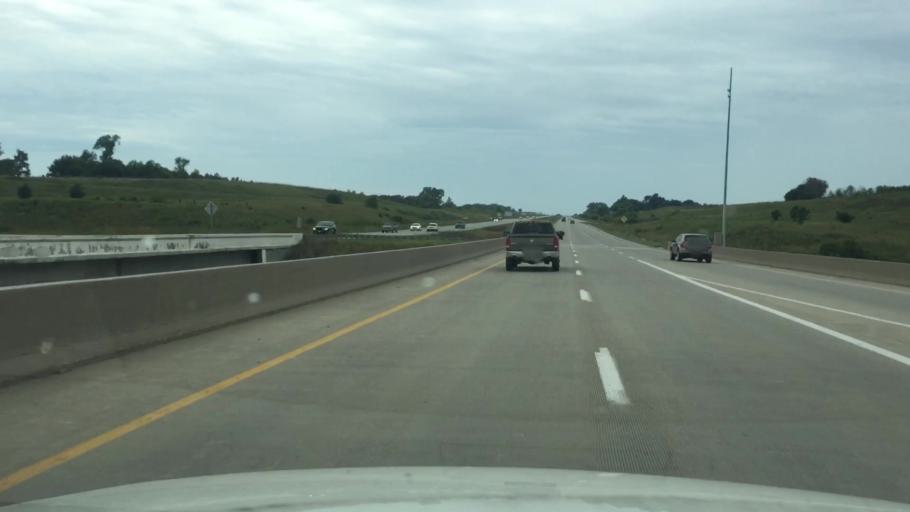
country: US
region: Iowa
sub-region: Warren County
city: Norwalk
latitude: 41.5141
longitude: -93.6818
